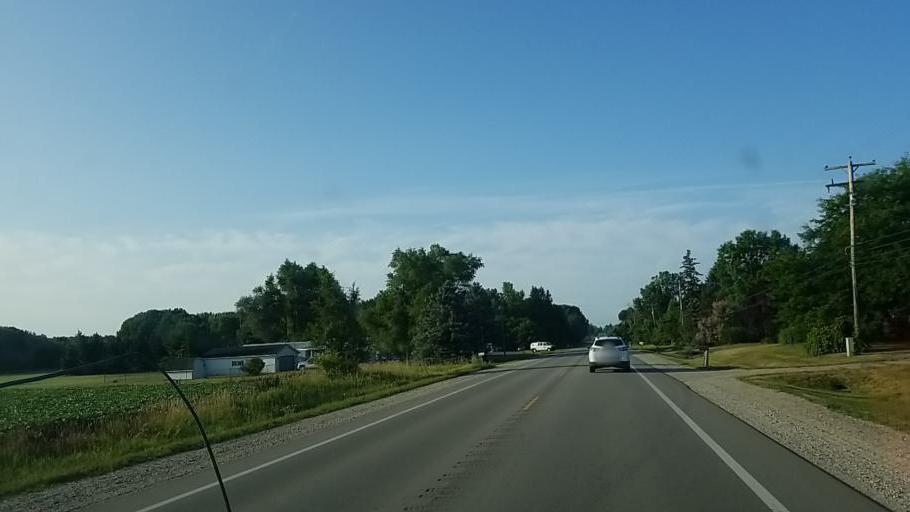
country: US
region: Michigan
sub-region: Montcalm County
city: Stanton
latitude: 43.2322
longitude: -85.0736
